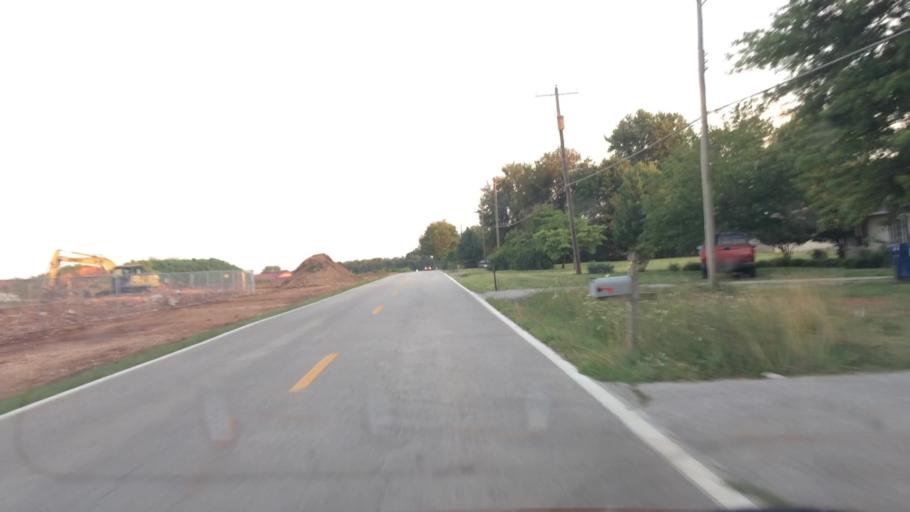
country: US
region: Missouri
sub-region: Greene County
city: Springfield
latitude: 37.2037
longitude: -93.3742
